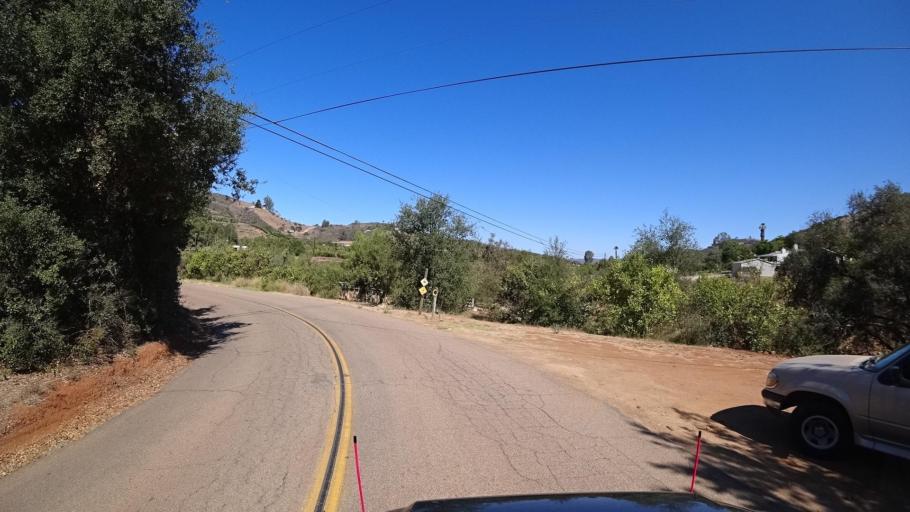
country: US
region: California
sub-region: San Diego County
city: Rainbow
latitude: 33.4180
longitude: -117.1760
